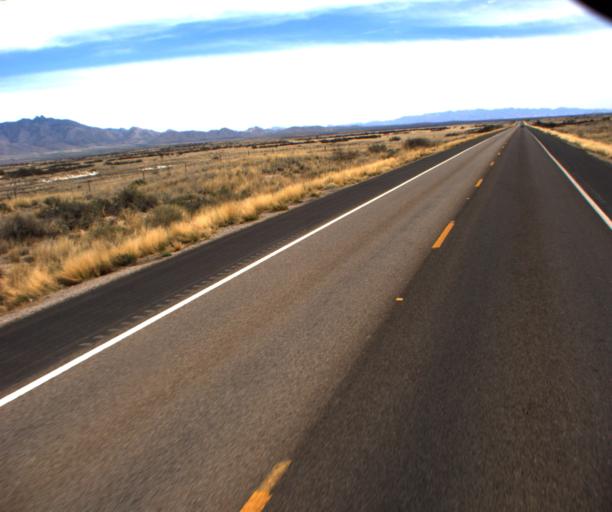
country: US
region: Arizona
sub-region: Cochise County
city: Willcox
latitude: 32.2292
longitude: -109.7998
